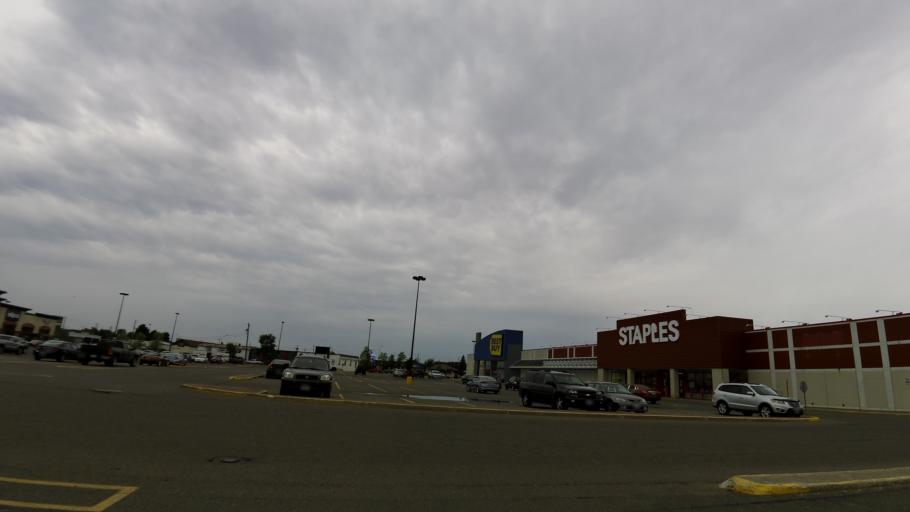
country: CA
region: Ontario
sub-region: Thunder Bay District
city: Thunder Bay
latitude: 48.4123
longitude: -89.2418
